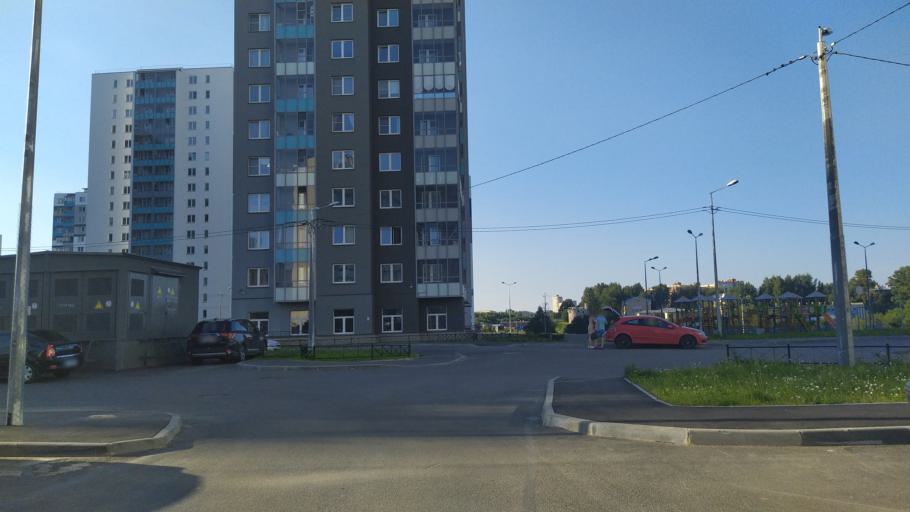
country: RU
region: Leningrad
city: Murino
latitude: 60.0336
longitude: 30.4595
